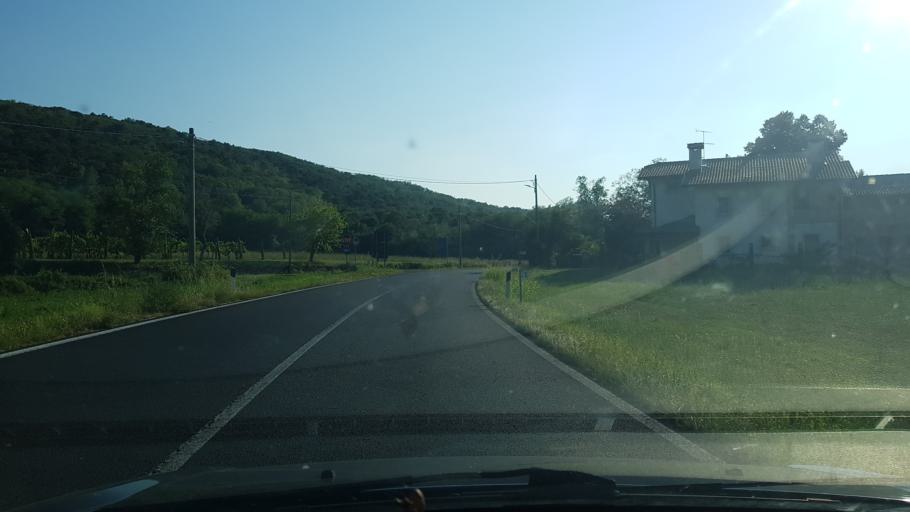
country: IT
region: Friuli Venezia Giulia
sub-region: Provincia di Gorizia
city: Farra d'Isonzo
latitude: 45.8953
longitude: 13.5388
